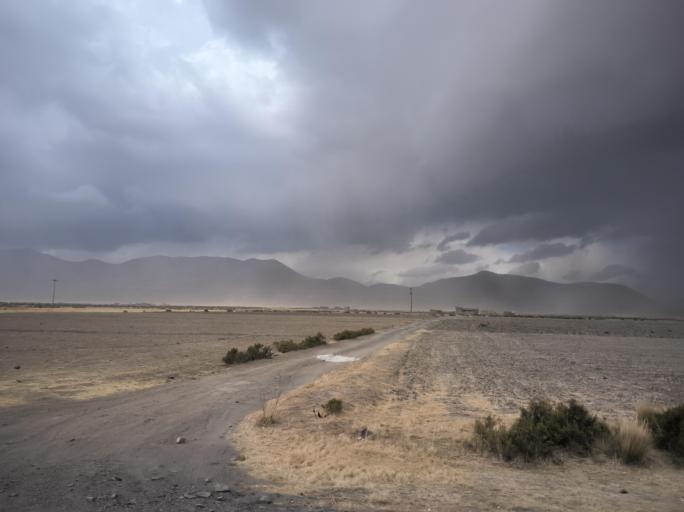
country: BO
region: Oruro
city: Challapata
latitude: -18.7780
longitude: -66.8522
